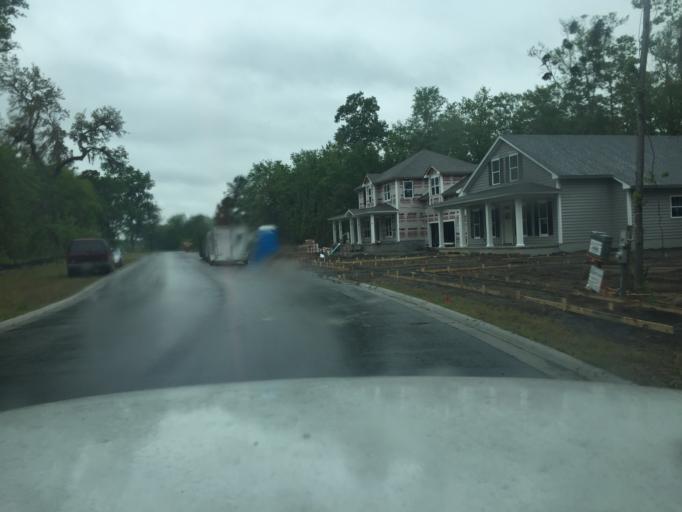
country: US
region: Georgia
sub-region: Chatham County
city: Georgetown
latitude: 32.0425
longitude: -81.2316
